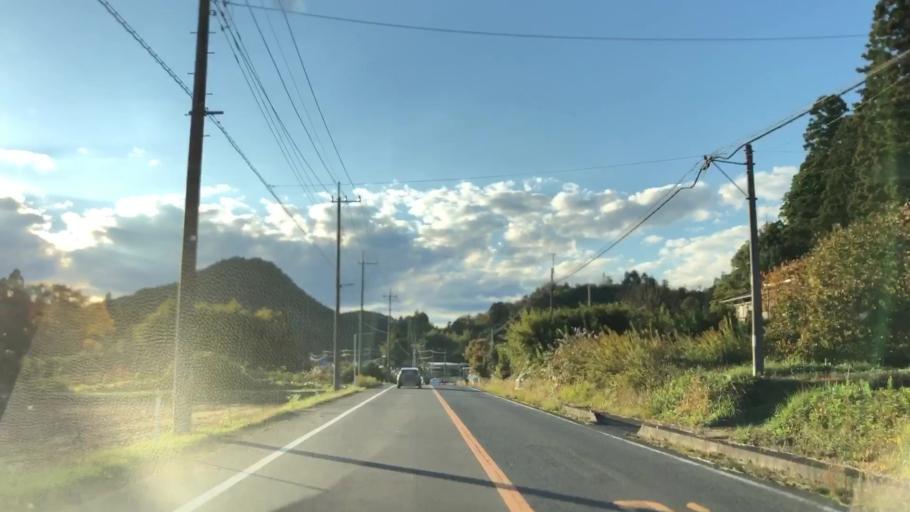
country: JP
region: Tochigi
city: Motegi
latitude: 36.4944
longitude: 140.2618
